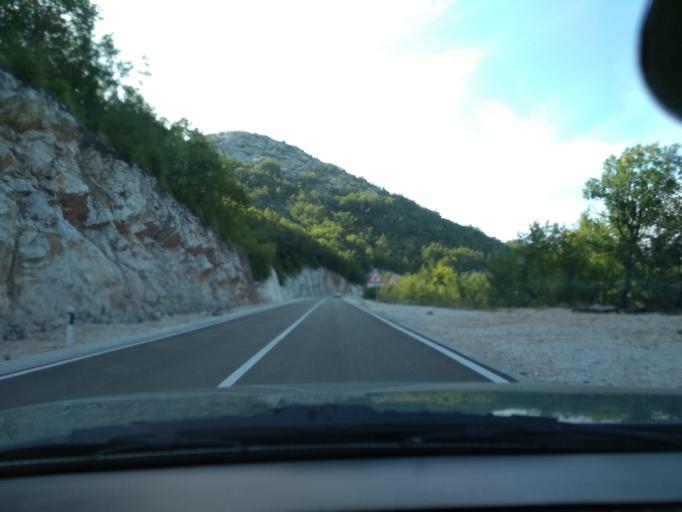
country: ME
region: Cetinje
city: Cetinje
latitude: 42.4192
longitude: 18.8756
